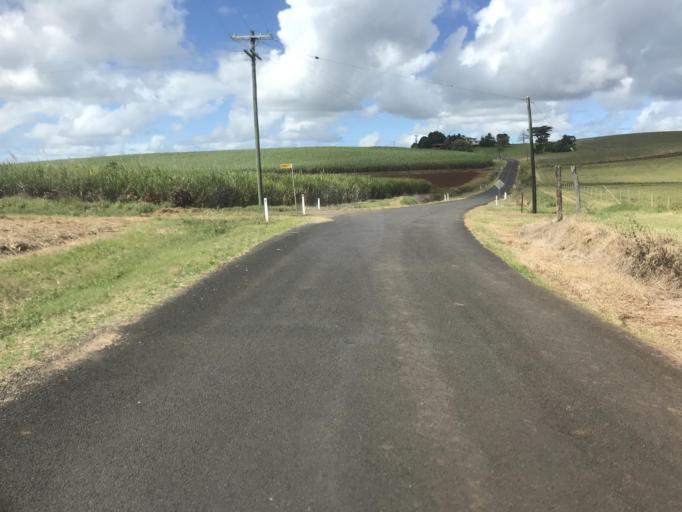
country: AU
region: Queensland
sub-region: Cassowary Coast
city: Innisfail
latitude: -17.5531
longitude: 145.8866
